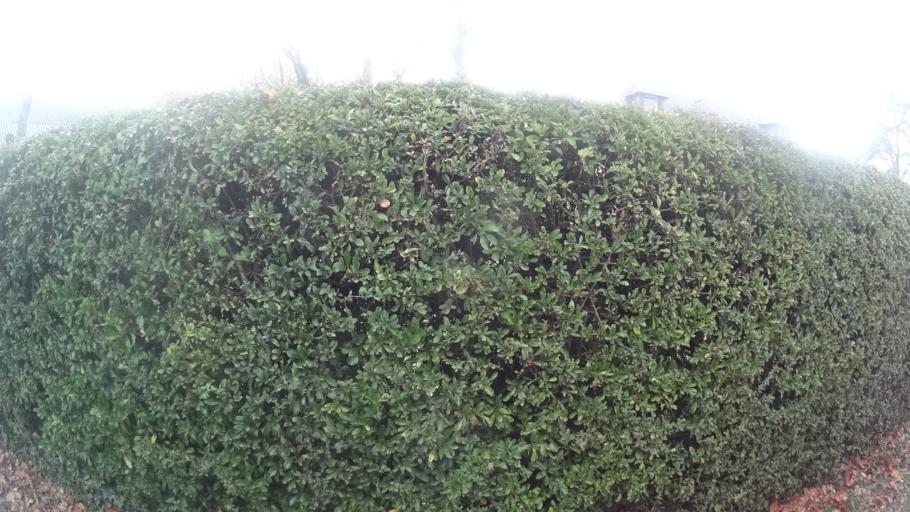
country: FR
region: Pays de la Loire
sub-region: Departement de la Loire-Atlantique
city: Avessac
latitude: 47.6519
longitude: -1.9925
